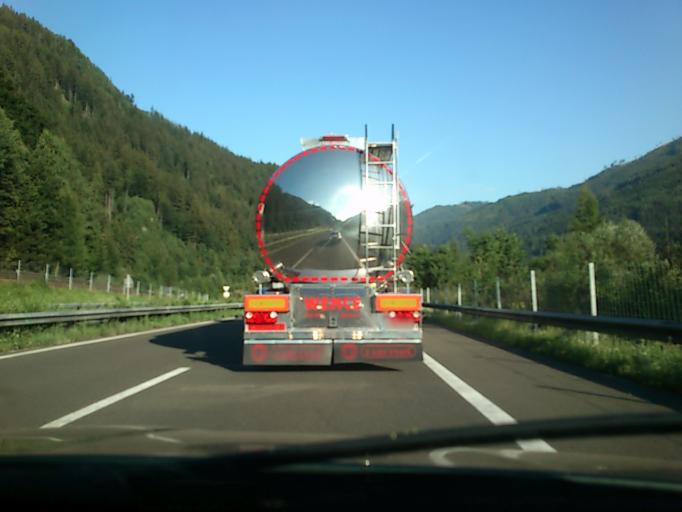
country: AT
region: Styria
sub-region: Politischer Bezirk Leoben
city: Wald am Schoberpass
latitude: 47.4353
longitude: 14.6998
